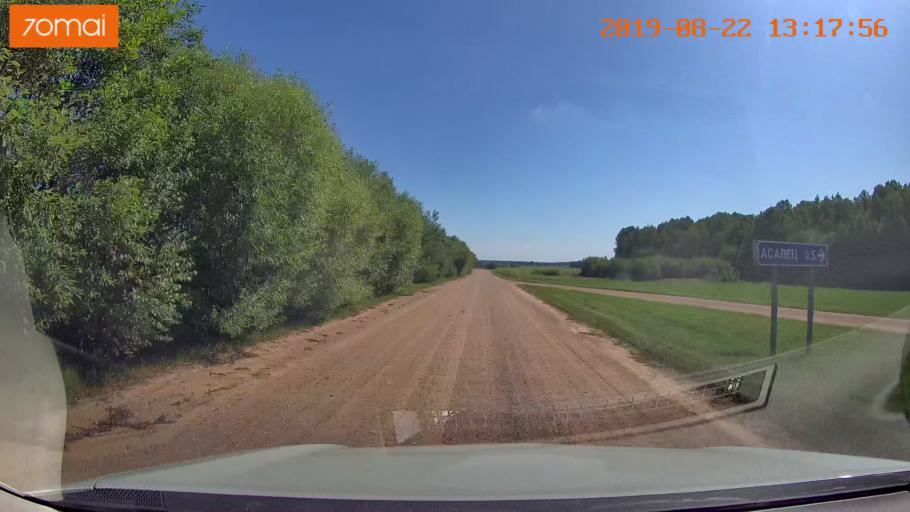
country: BY
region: Minsk
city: Prawdzinski
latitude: 53.2440
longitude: 27.9306
